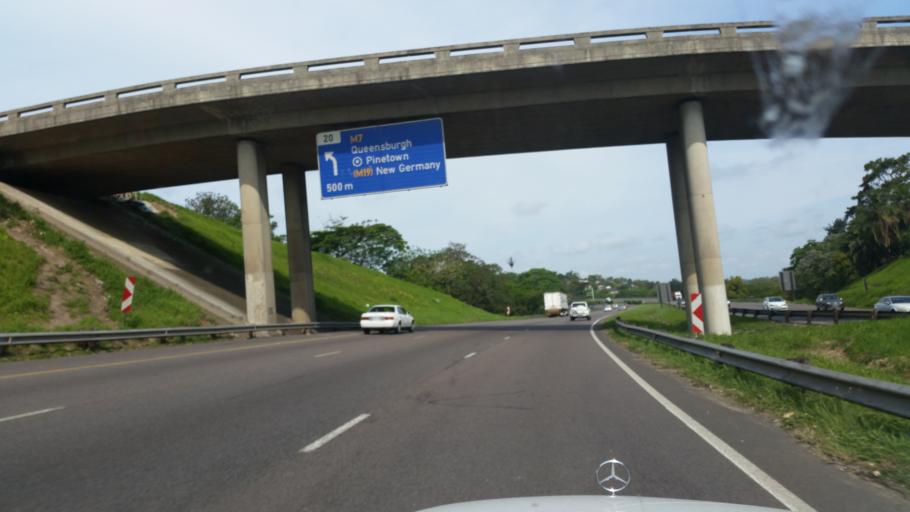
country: ZA
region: KwaZulu-Natal
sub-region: eThekwini Metropolitan Municipality
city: Berea
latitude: -29.8339
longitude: 30.8519
